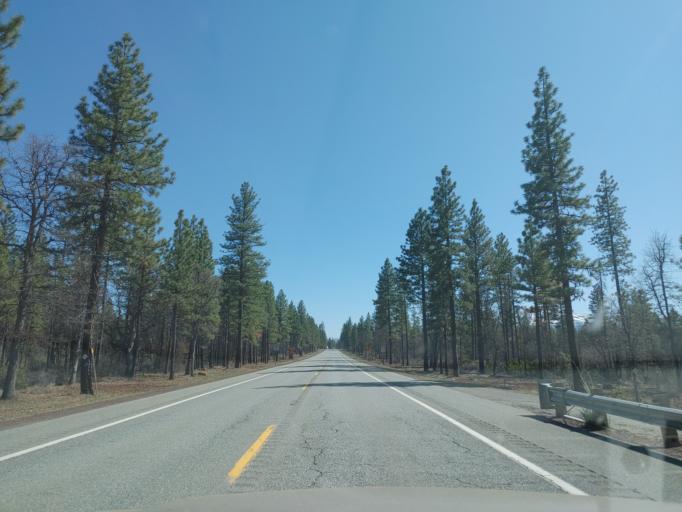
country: US
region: California
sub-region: Shasta County
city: Burney
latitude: 40.9465
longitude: -121.6099
